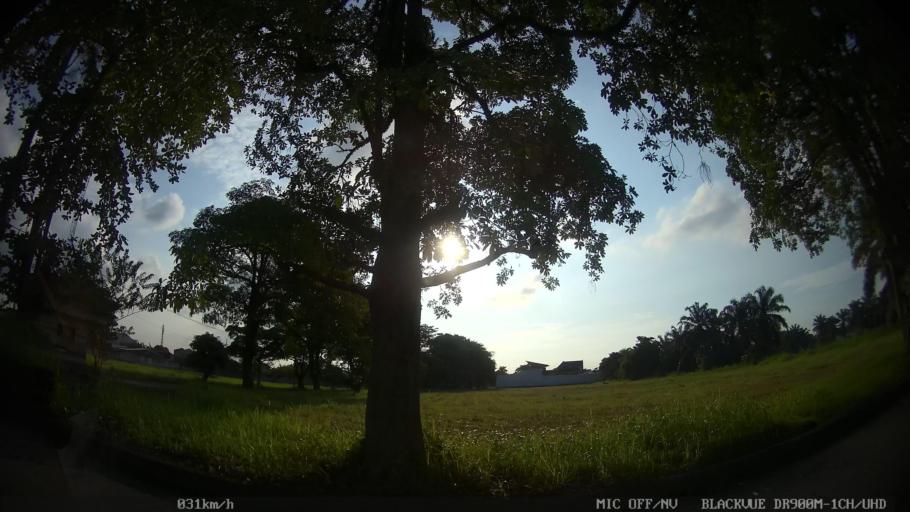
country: ID
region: North Sumatra
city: Medan
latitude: 3.6203
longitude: 98.6530
